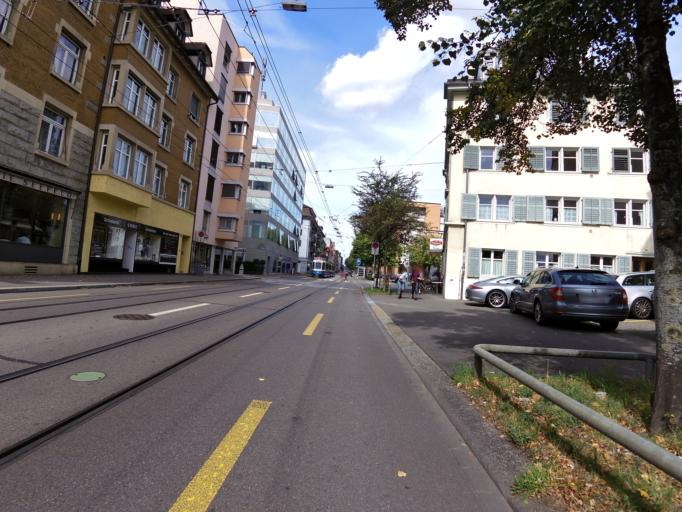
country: CH
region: Zurich
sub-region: Bezirk Zuerich
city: Zuerich (Kreis 8)
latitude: 47.3526
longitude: 8.5594
